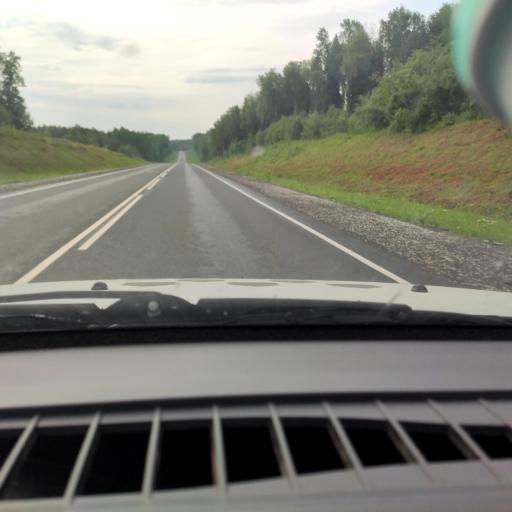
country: RU
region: Kirov
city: Kostino
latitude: 58.6652
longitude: 53.7604
